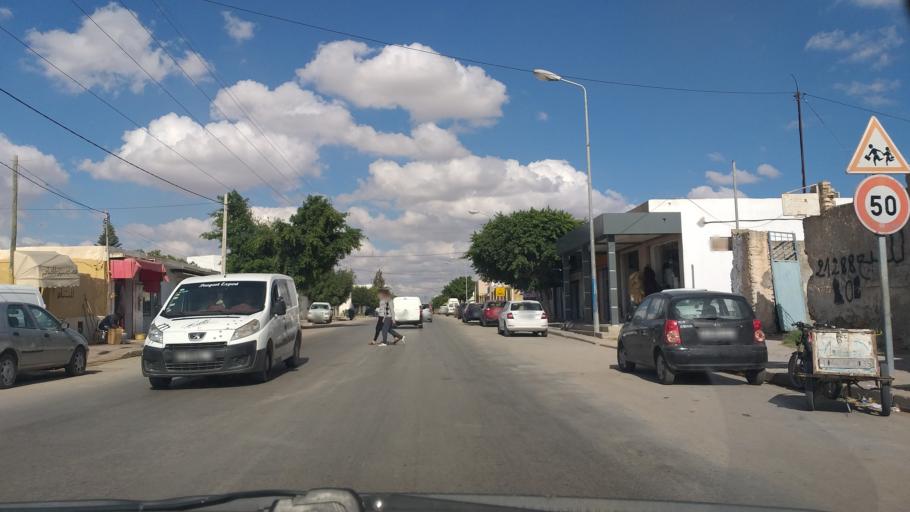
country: TN
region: Safaqis
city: Al Qarmadah
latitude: 34.7707
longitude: 10.7748
